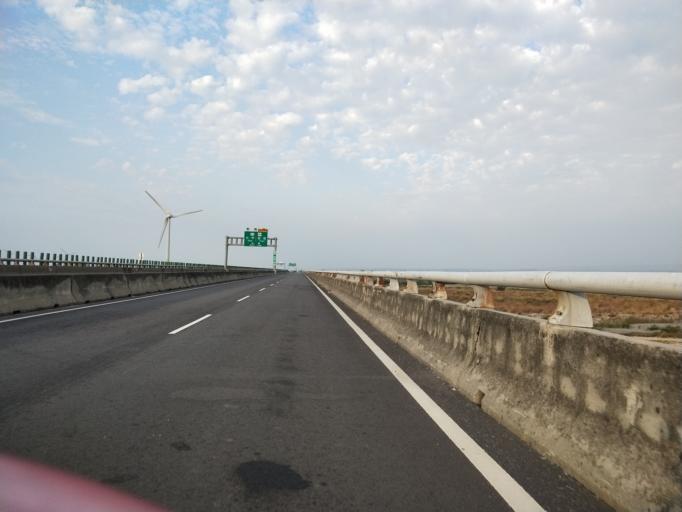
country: TW
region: Taiwan
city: Fengyuan
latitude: 24.3988
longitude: 120.6087
